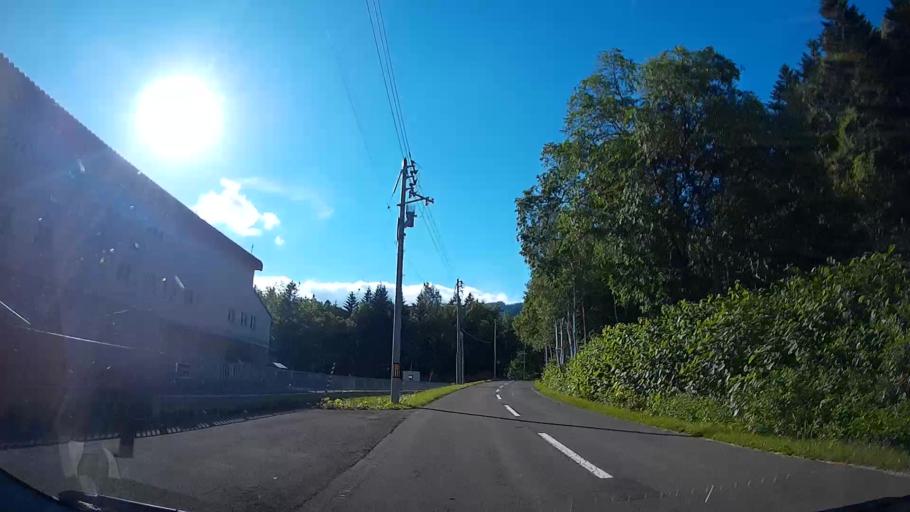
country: JP
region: Hokkaido
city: Otaru
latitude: 42.9857
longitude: 141.1224
